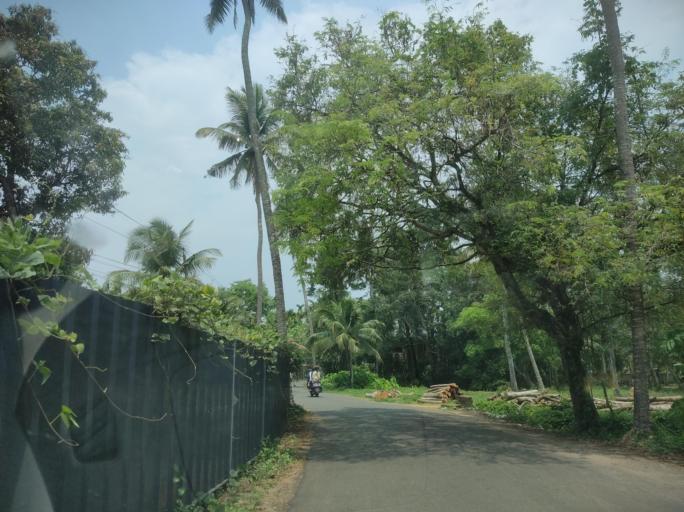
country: IN
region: Kerala
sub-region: Alappuzha
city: Vayalar
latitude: 9.7360
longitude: 76.3279
